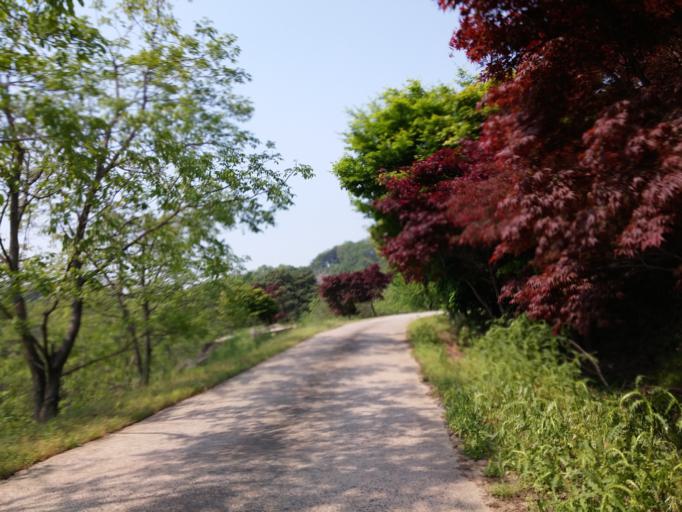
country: KR
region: Chungcheongbuk-do
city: Okcheon
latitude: 36.3837
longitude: 127.6046
